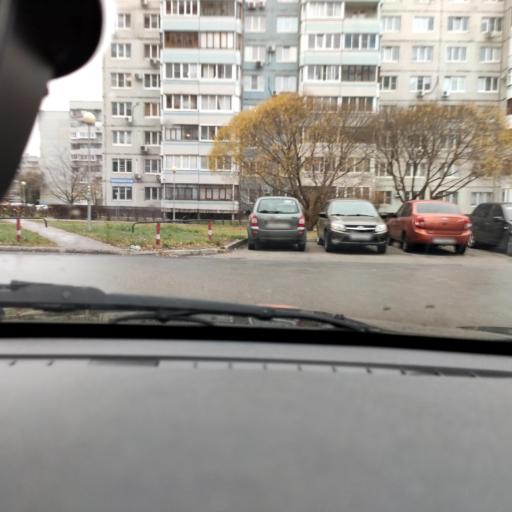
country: RU
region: Samara
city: Tol'yatti
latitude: 53.5344
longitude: 49.3427
